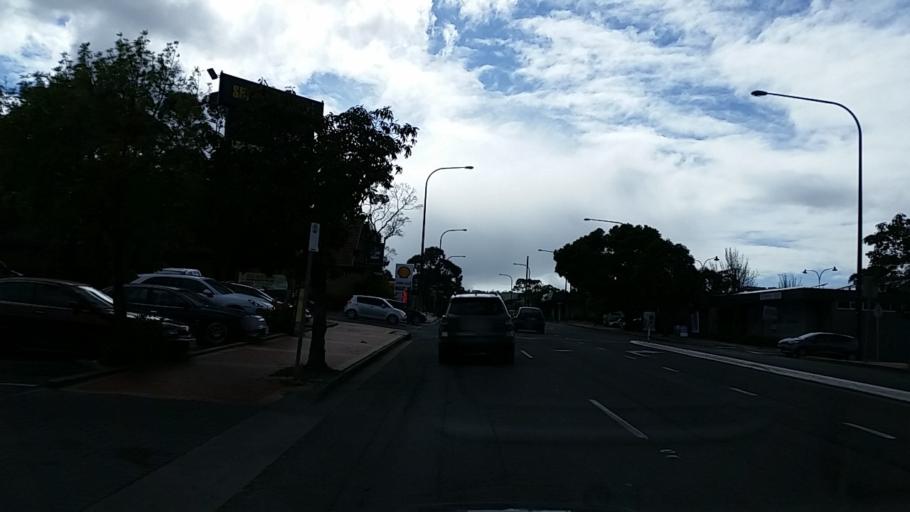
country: AU
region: South Australia
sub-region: Mitcham
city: Blackwood
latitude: -35.0213
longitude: 138.6142
